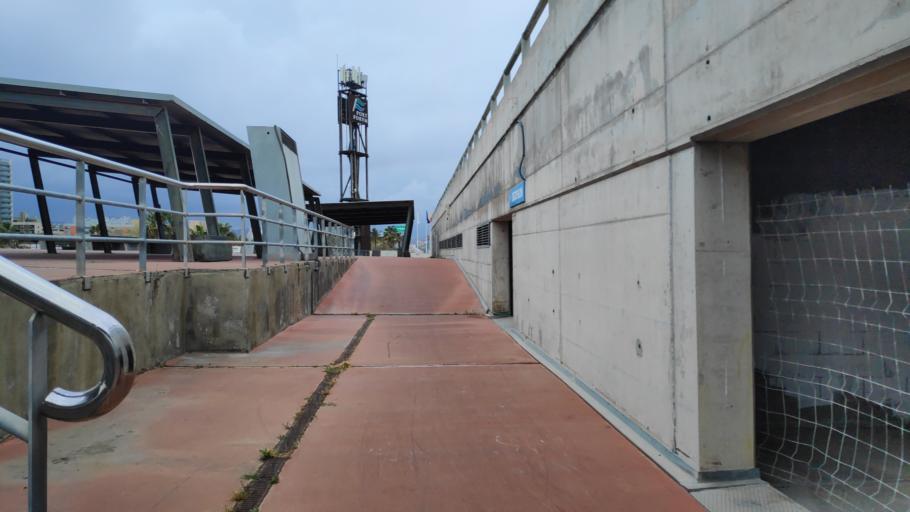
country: ES
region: Catalonia
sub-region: Provincia de Barcelona
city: Sant Adria de Besos
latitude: 41.4150
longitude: 2.2286
